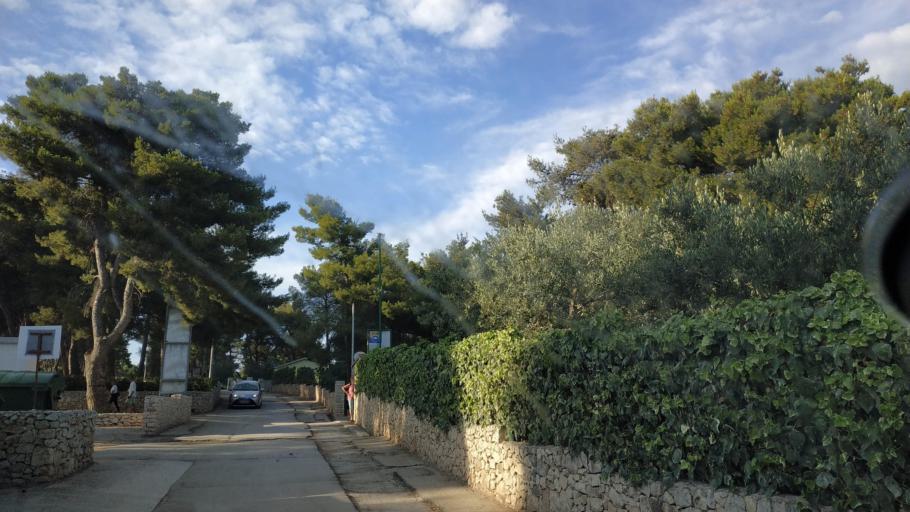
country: HR
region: Splitsko-Dalmatinska
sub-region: Grad Trogir
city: Trogir
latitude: 43.4817
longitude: 16.2443
